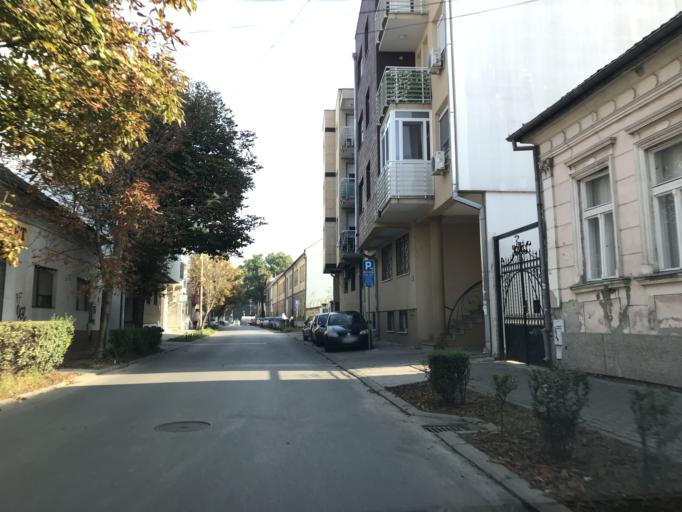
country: RS
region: Autonomna Pokrajina Vojvodina
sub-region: Juznobacki Okrug
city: Novi Sad
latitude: 45.2512
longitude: 19.8315
